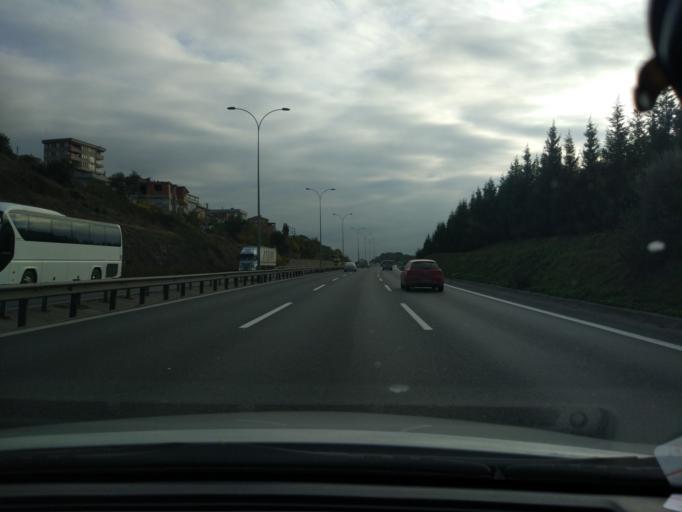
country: TR
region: Kocaeli
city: Korfez
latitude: 40.7788
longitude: 29.7173
